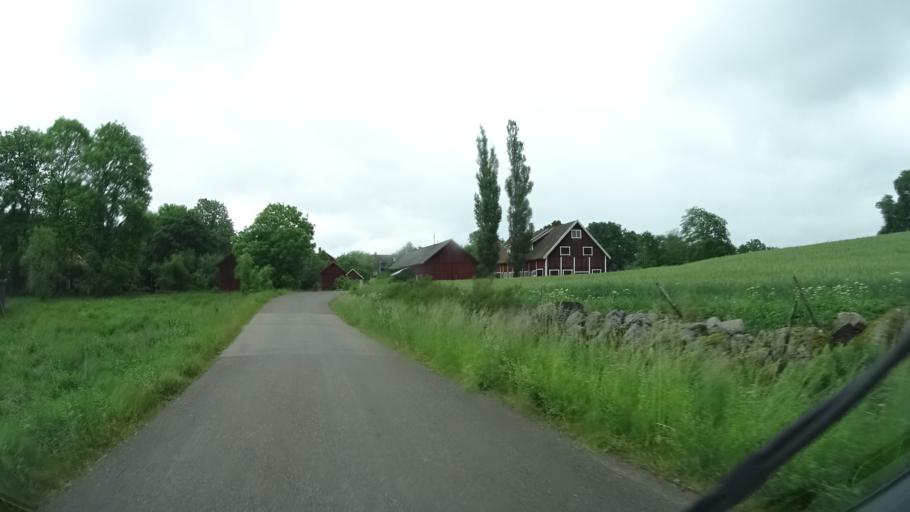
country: SE
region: Joenkoeping
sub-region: Eksjo Kommun
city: Mariannelund
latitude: 57.6820
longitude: 15.5774
